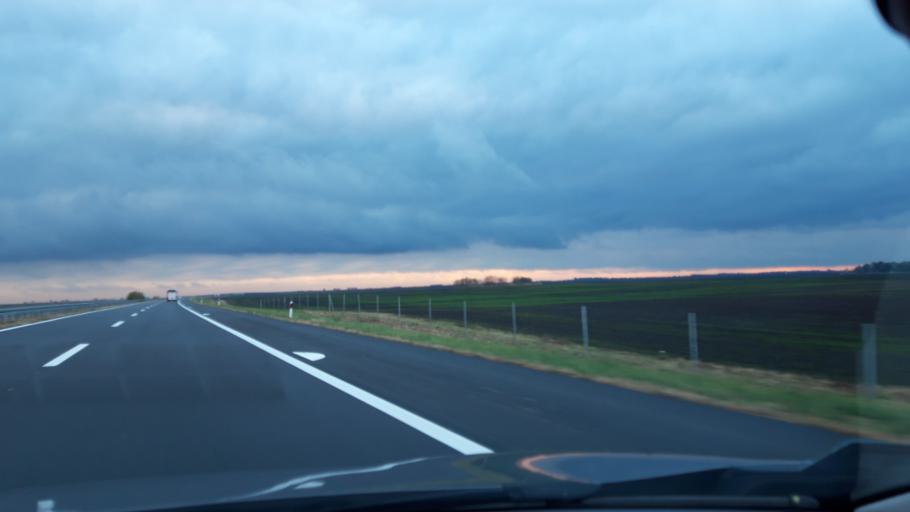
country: RS
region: Autonomna Pokrajina Vojvodina
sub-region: Severnobacki Okrug
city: Backa Topola
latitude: 45.7786
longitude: 19.6991
